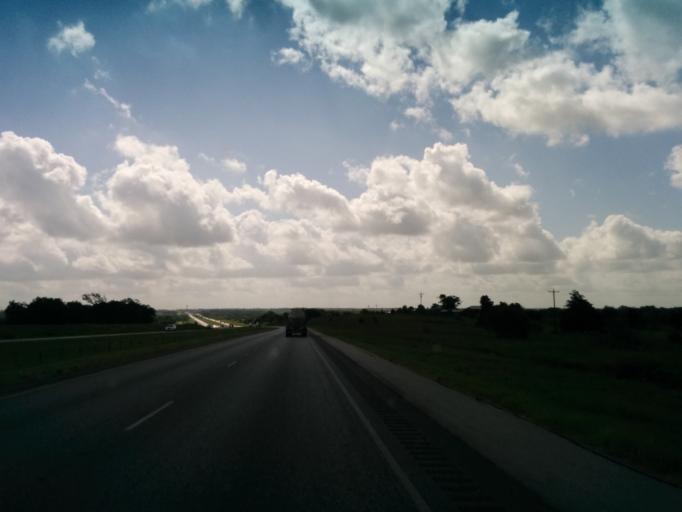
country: US
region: Texas
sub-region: Fayette County
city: Schulenburg
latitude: 29.6889
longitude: -96.9601
